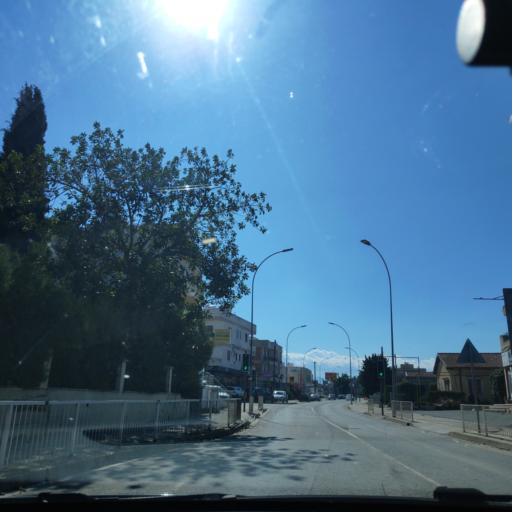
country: CY
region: Lefkosia
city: Kato Deftera
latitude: 35.1102
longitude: 33.3056
